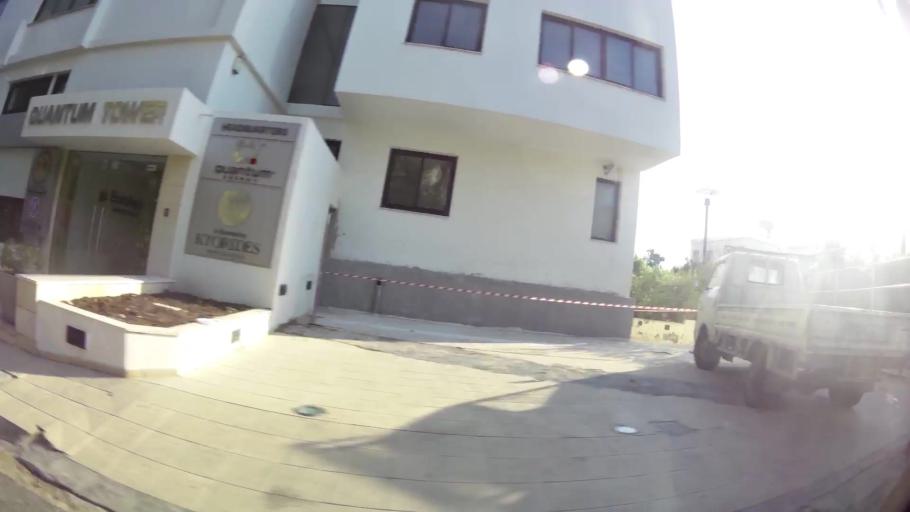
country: CY
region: Lefkosia
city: Nicosia
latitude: 35.1751
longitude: 33.3395
